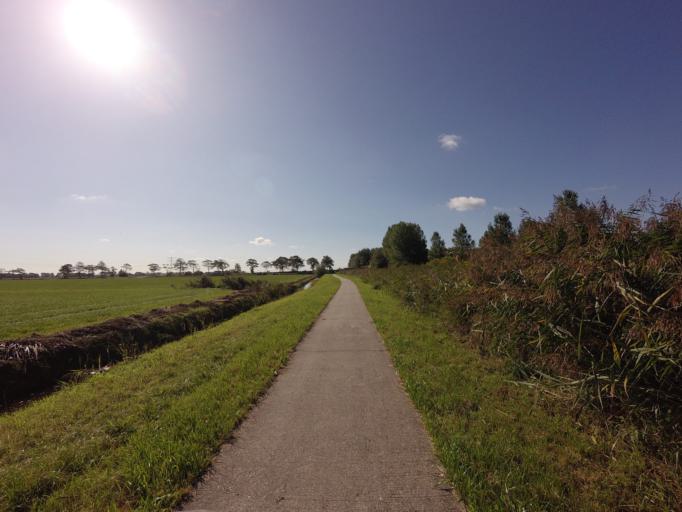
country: NL
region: Friesland
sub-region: Gemeente Leeuwarden
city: Wirdum
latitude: 53.1506
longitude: 5.7639
